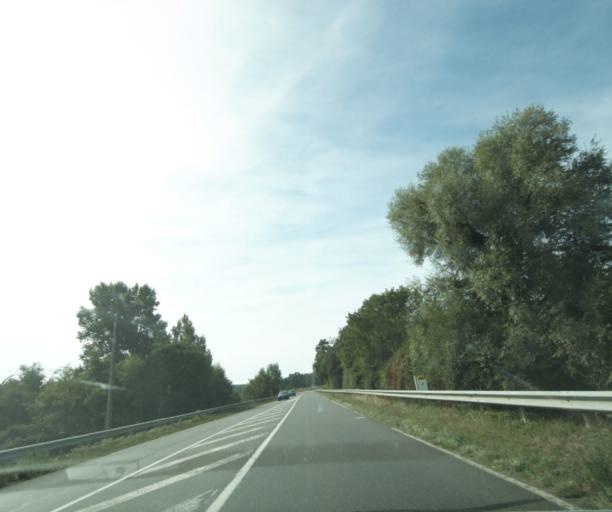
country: FR
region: Auvergne
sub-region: Departement de l'Allier
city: Saint-Germain-des-Fosses
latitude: 46.1875
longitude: 3.4866
